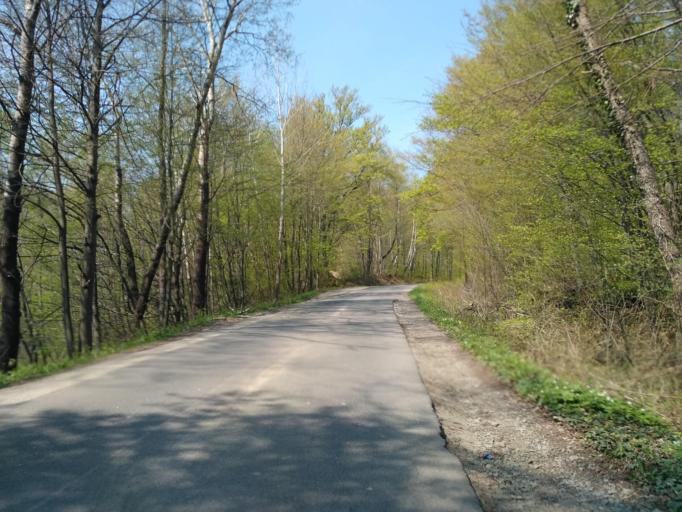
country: PL
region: Subcarpathian Voivodeship
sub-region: Powiat krosnienski
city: Chorkowka
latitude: 49.6143
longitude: 21.7165
